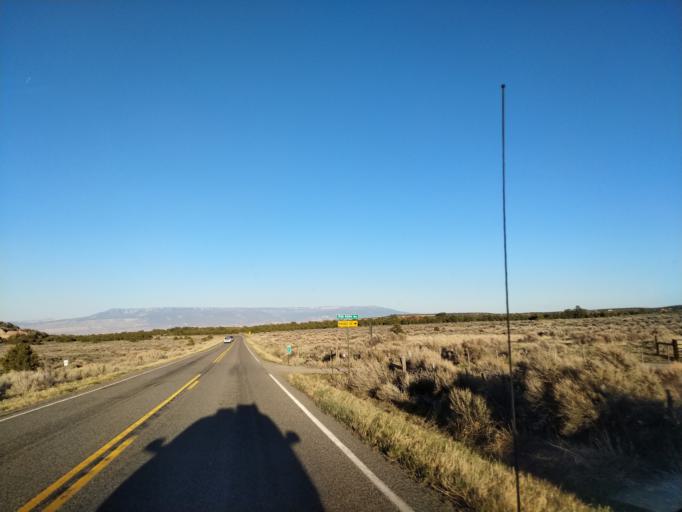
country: US
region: Colorado
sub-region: Mesa County
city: Redlands
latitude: 39.0047
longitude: -108.6957
